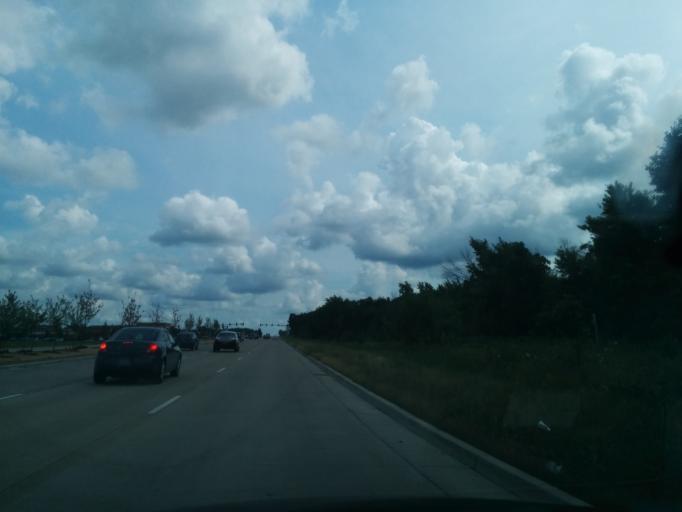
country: US
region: Illinois
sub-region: Cook County
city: Orland Hills
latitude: 41.5825
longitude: -87.8523
